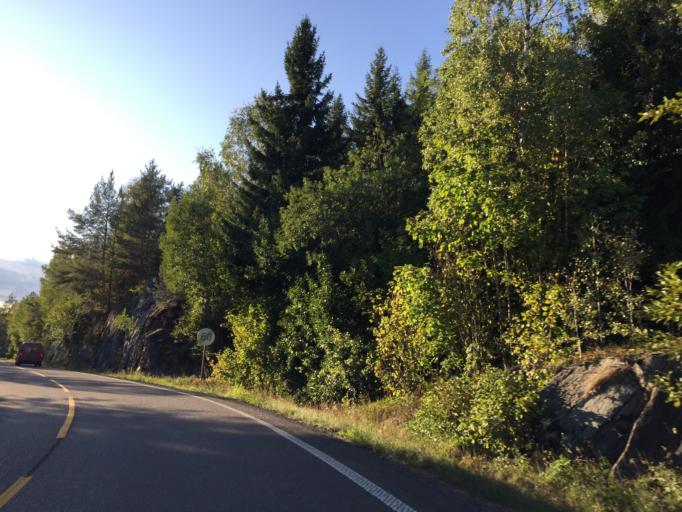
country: NO
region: Akershus
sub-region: Enebakk
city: Flateby
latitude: 59.8055
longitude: 11.2576
